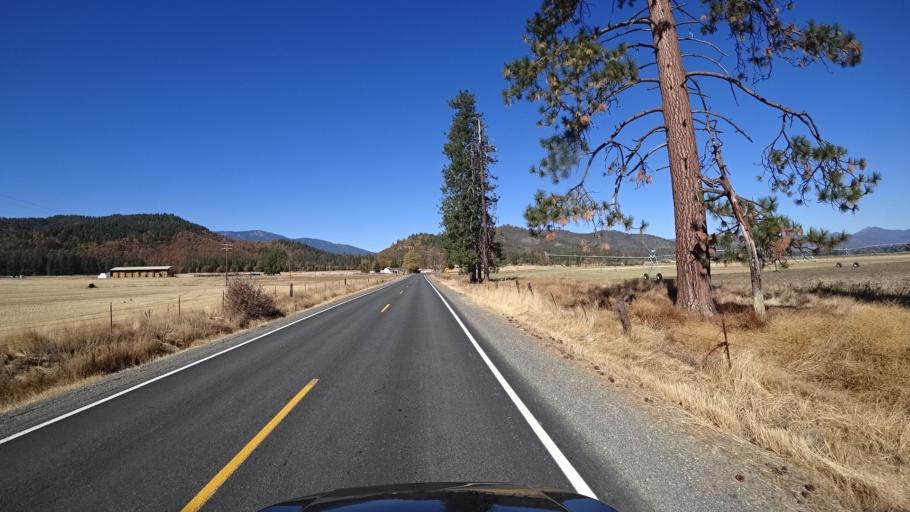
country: US
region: California
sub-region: Siskiyou County
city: Yreka
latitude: 41.5568
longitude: -122.9214
